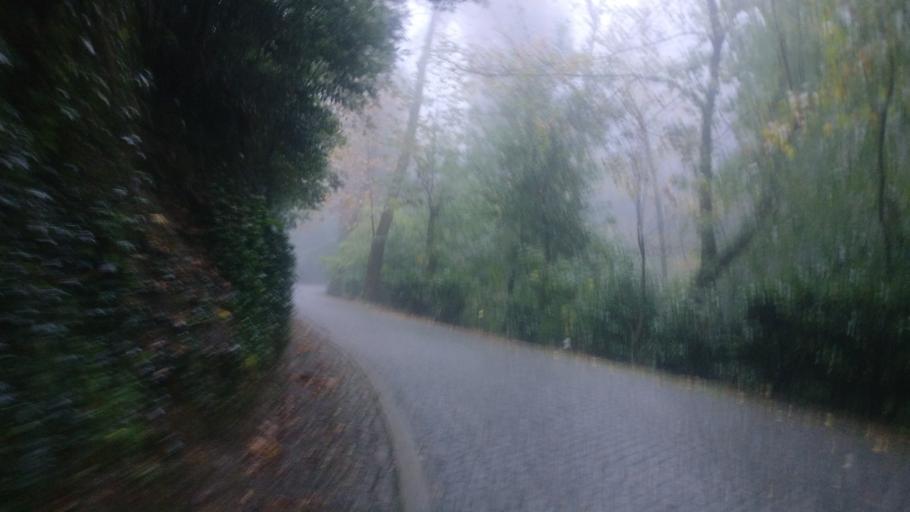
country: PT
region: Aveiro
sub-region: Mealhada
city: Pampilhosa do Botao
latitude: 40.3776
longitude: -8.3640
